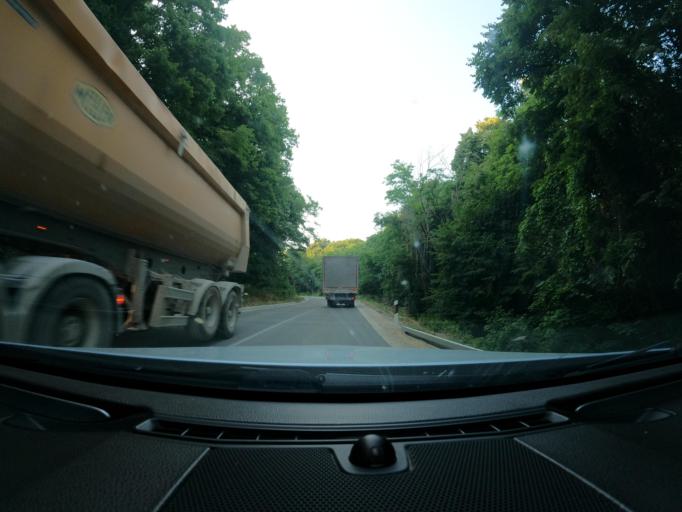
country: RS
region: Autonomna Pokrajina Vojvodina
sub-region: Juznobacki Okrug
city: Beocin
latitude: 45.1384
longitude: 19.7231
